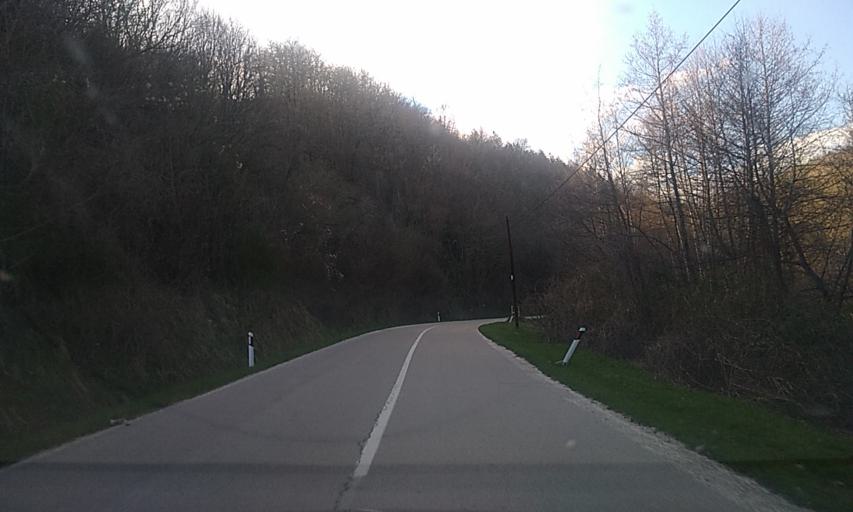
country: RS
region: Central Serbia
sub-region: Pcinjski Okrug
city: Bosilegrad
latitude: 42.4399
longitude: 22.5053
